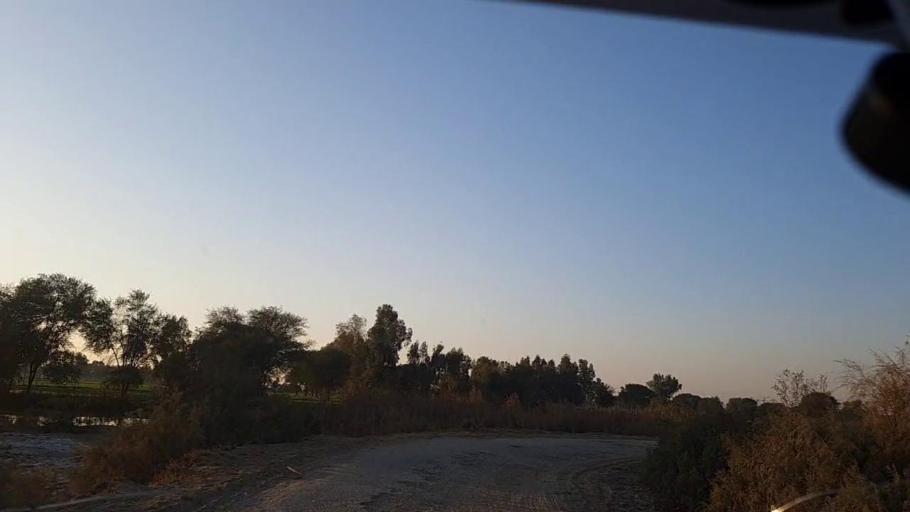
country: PK
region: Sindh
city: Khanpur
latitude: 27.8185
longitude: 69.2994
